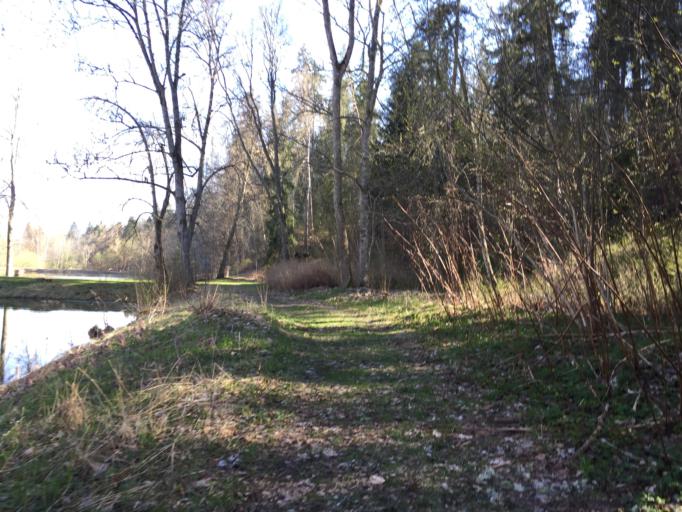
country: EE
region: Vorumaa
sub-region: Antsla vald
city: Vana-Antsla
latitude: 57.9015
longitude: 26.2785
